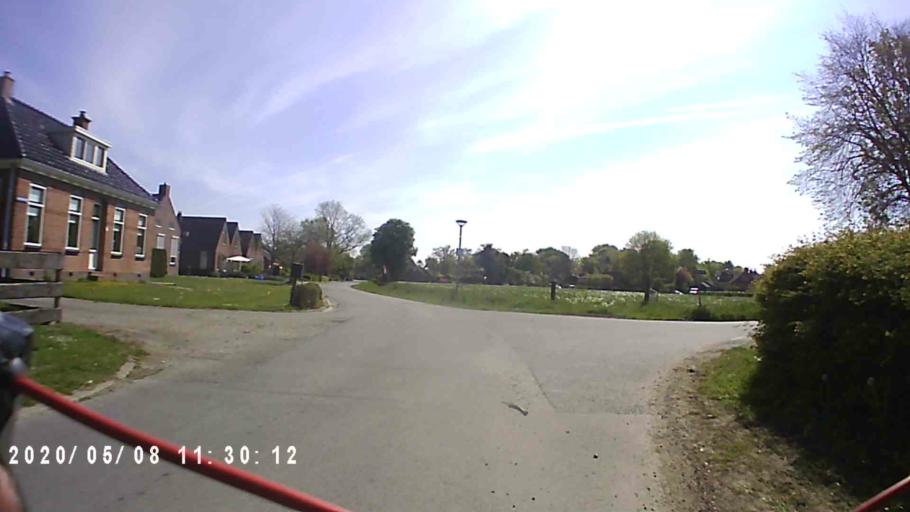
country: NL
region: Groningen
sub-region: Gemeente Bedum
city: Bedum
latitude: 53.3457
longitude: 6.7061
